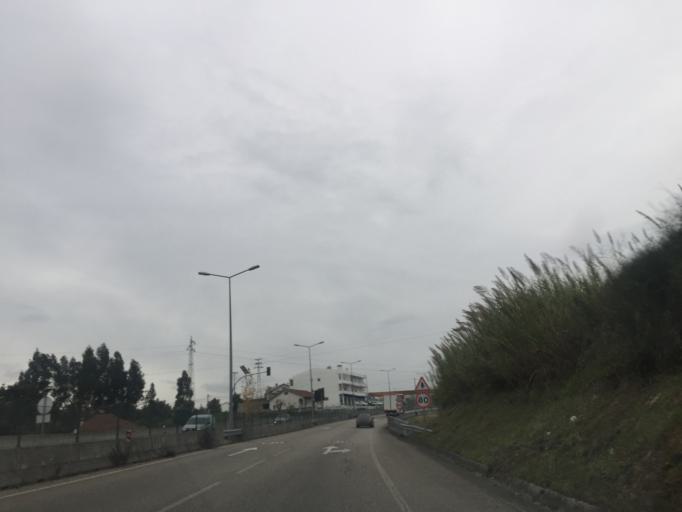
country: PT
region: Coimbra
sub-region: Coimbra
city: Coimbra
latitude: 40.1892
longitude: -8.4296
